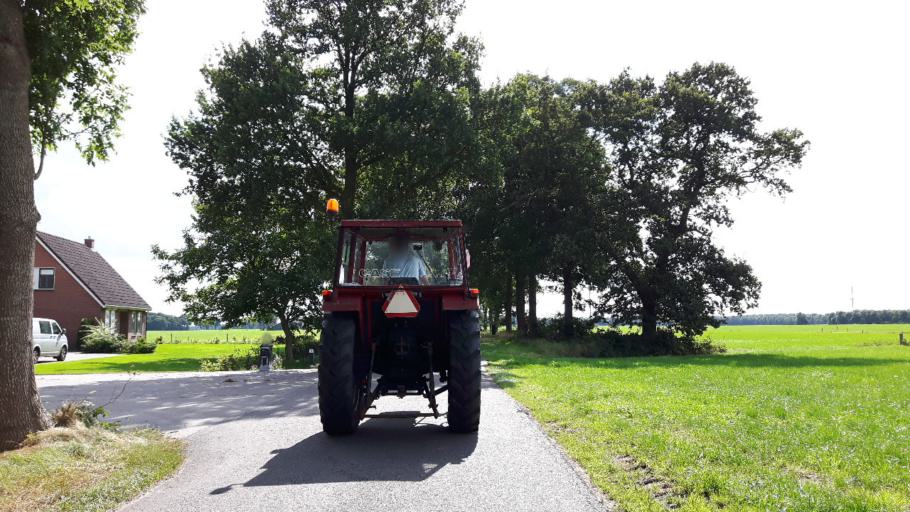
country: NL
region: Friesland
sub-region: Gemeente Heerenveen
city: Jubbega
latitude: 53.0188
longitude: 6.2631
